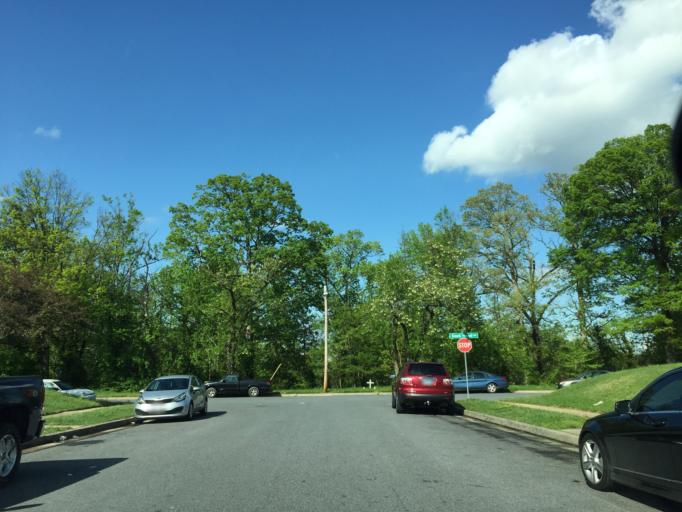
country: US
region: Maryland
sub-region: Baltimore County
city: Middle River
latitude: 39.3239
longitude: -76.4339
